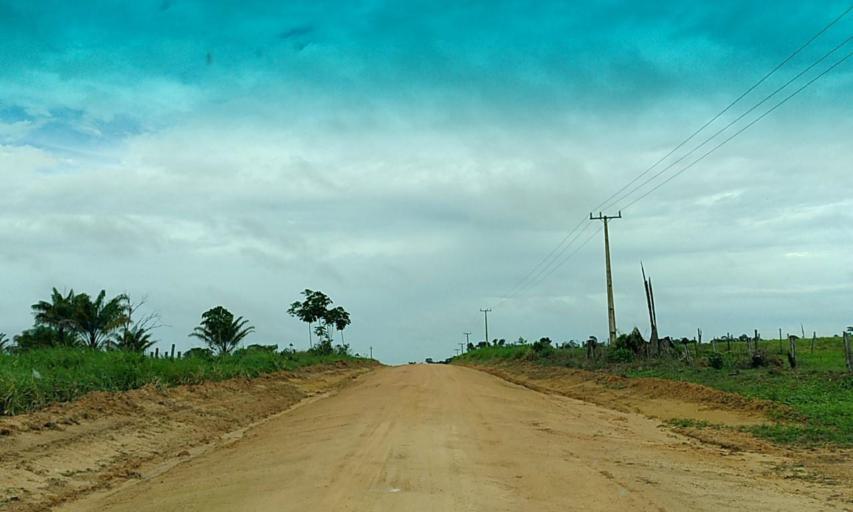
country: BR
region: Para
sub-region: Senador Jose Porfirio
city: Senador Jose Porfirio
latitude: -3.0269
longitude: -51.6811
